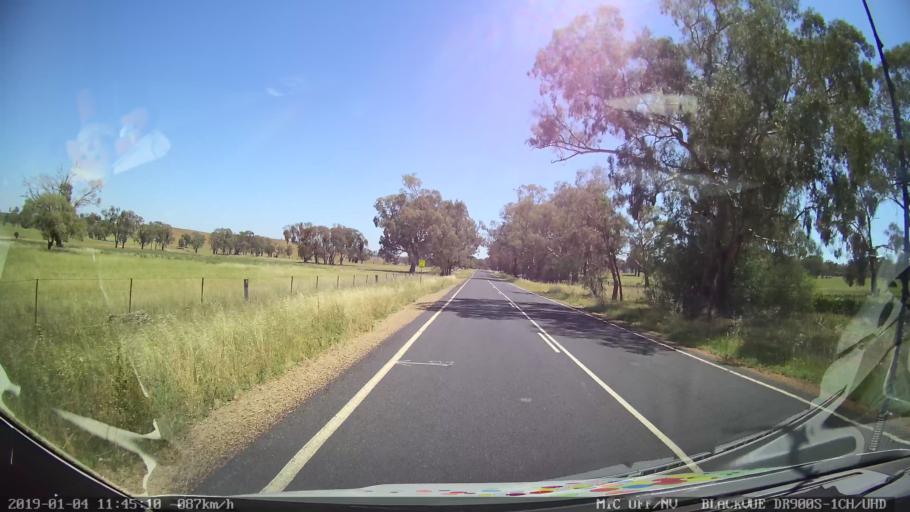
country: AU
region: New South Wales
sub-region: Cabonne
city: Molong
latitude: -32.9571
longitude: 148.7644
